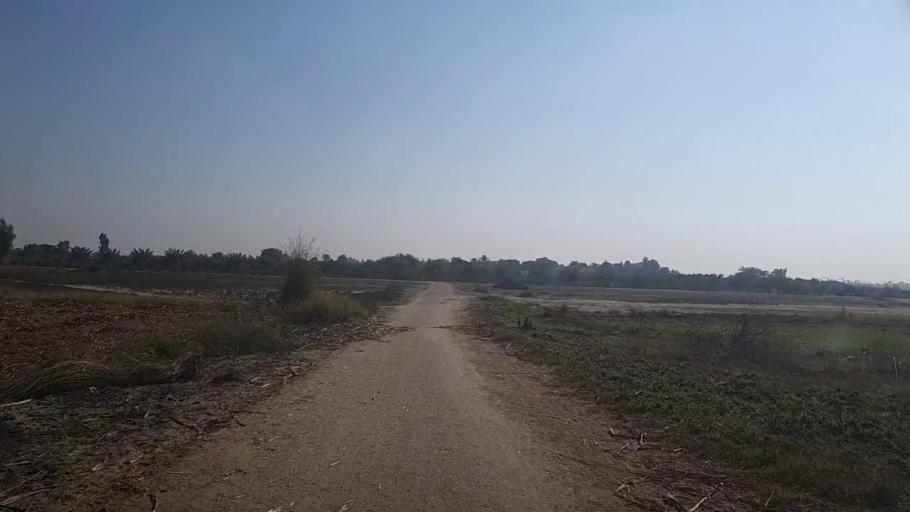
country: PK
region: Sindh
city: Kot Diji
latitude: 27.4306
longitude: 68.7340
